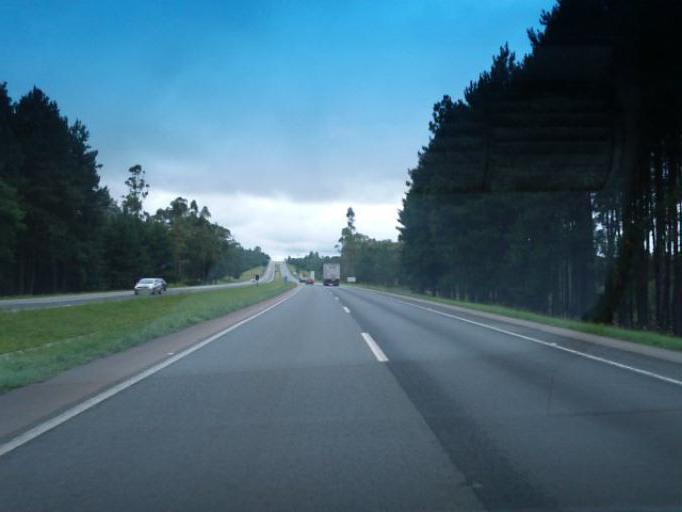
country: BR
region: Parana
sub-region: Piraquara
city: Piraquara
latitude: -25.4024
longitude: -49.0588
